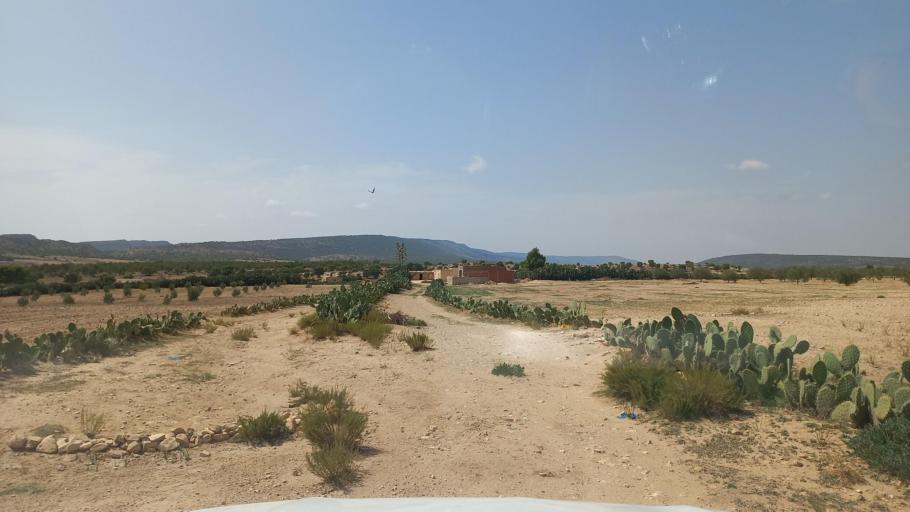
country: TN
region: Al Qasrayn
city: Sbiba
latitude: 35.3963
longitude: 8.9858
